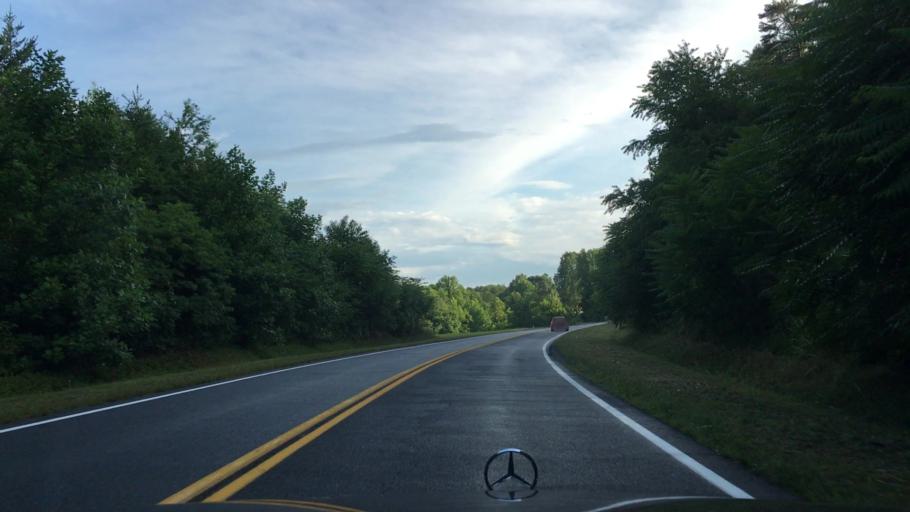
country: US
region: Virginia
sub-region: Campbell County
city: Altavista
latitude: 37.1673
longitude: -79.2960
